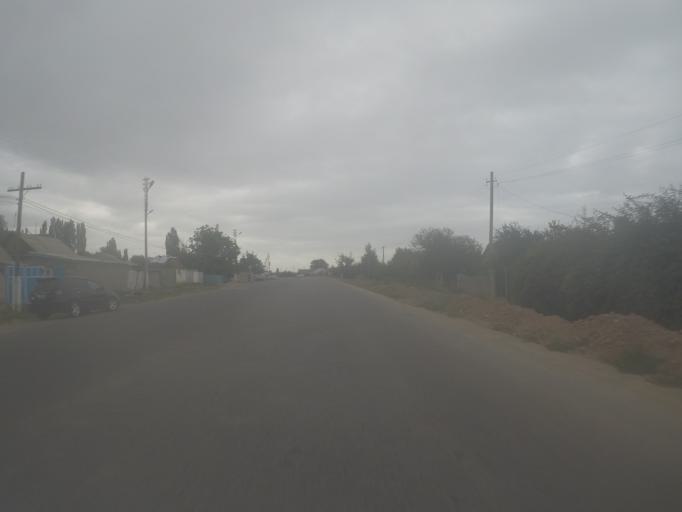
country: KG
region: Ysyk-Koel
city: Cholpon-Ata
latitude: 42.6908
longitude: 77.3610
